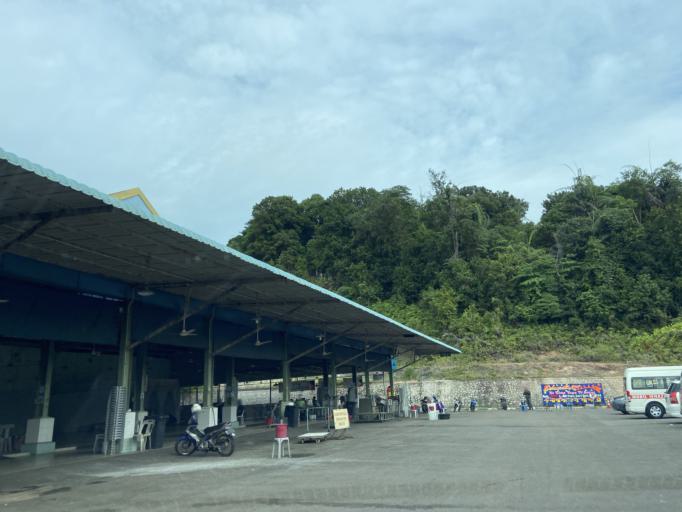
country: SG
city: Singapore
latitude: 1.1214
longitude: 104.0084
